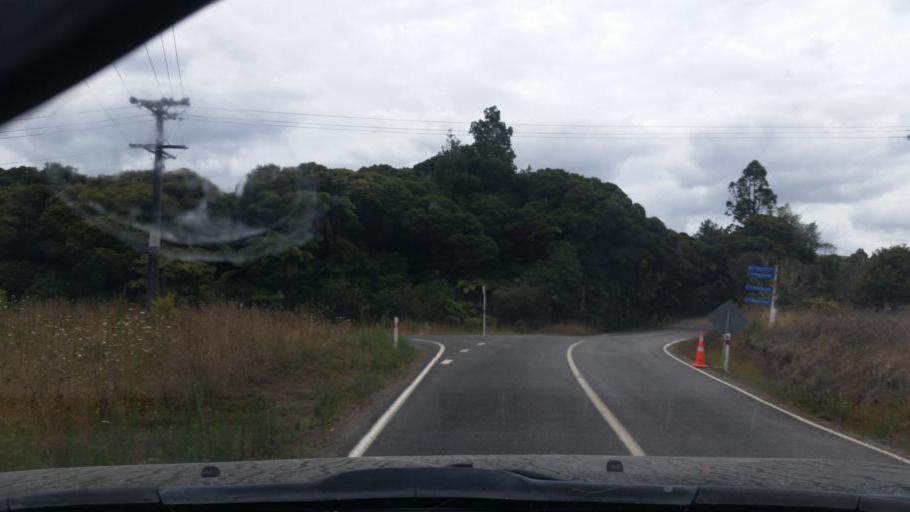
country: NZ
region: Northland
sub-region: Kaipara District
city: Dargaville
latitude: -35.7196
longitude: 173.6523
